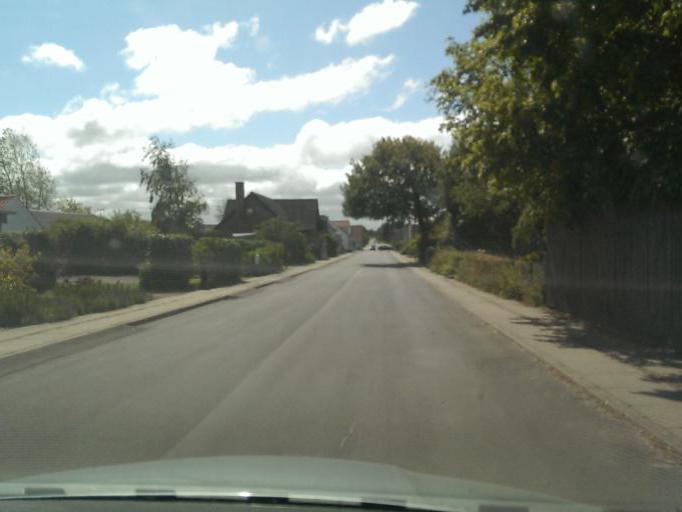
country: DK
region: North Denmark
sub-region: Jammerbugt Kommune
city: Pandrup
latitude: 57.2502
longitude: 9.6167
